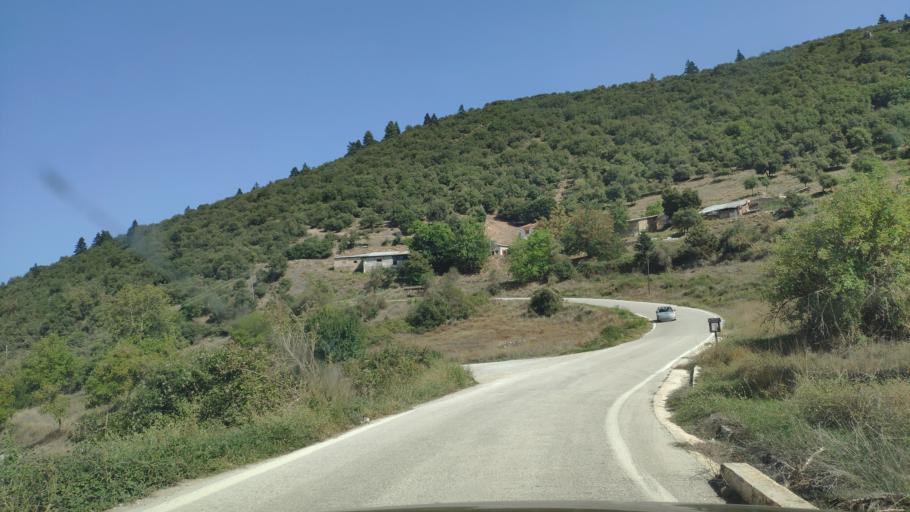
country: GR
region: West Greece
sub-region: Nomos Achaias
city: Aiyira
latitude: 37.9158
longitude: 22.3299
